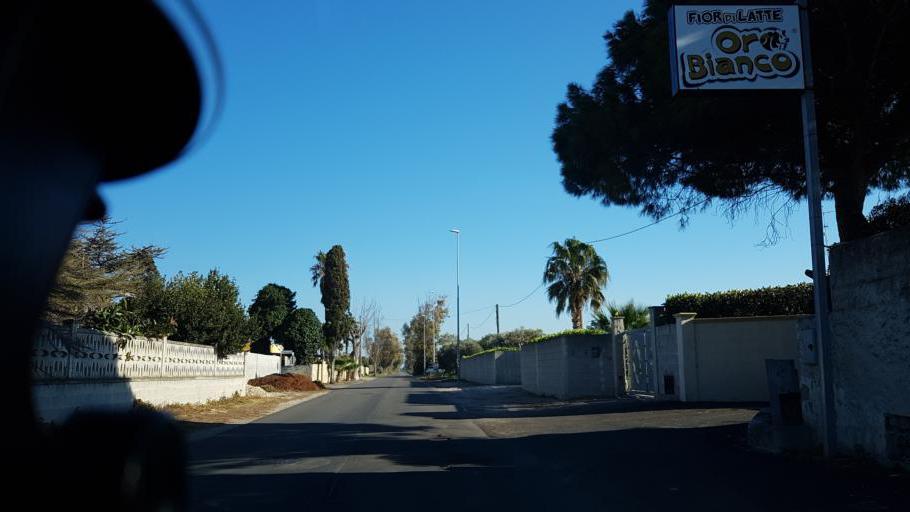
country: IT
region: Apulia
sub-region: Provincia di Lecce
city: Merine
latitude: 40.4253
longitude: 18.2449
